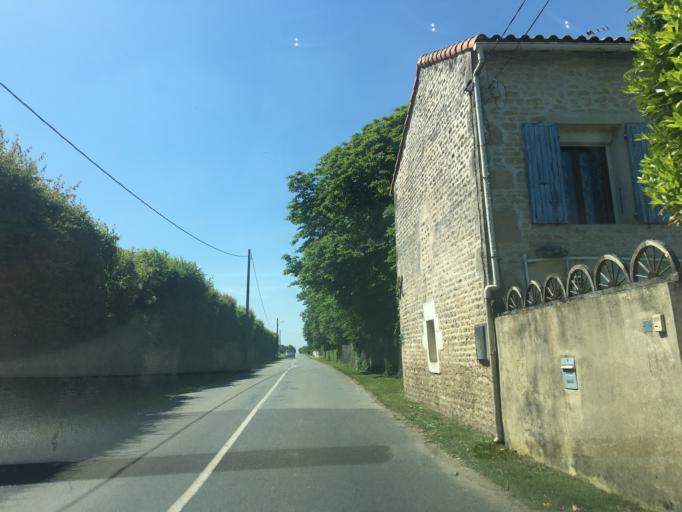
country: FR
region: Poitou-Charentes
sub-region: Departement des Deux-Sevres
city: Beauvoir-sur-Niort
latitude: 46.0739
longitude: -0.5081
